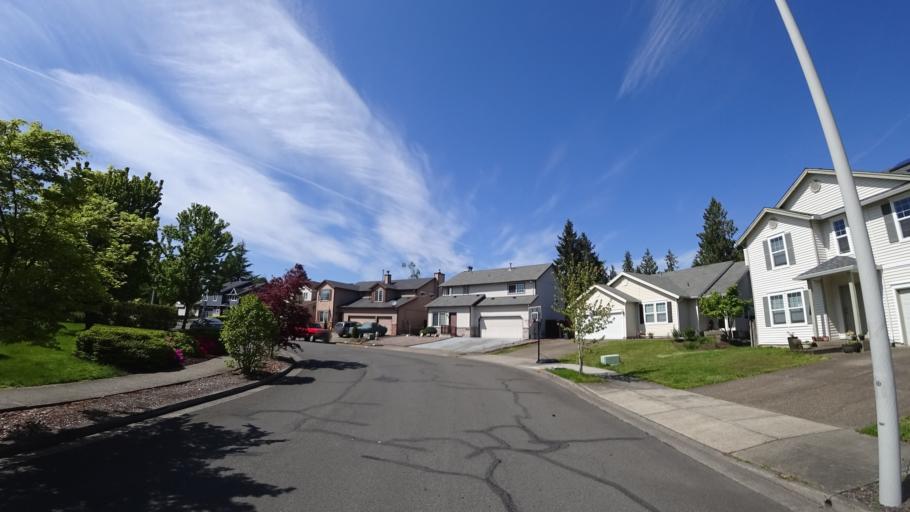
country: US
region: Oregon
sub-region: Washington County
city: Hillsboro
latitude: 45.5079
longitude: -122.9494
